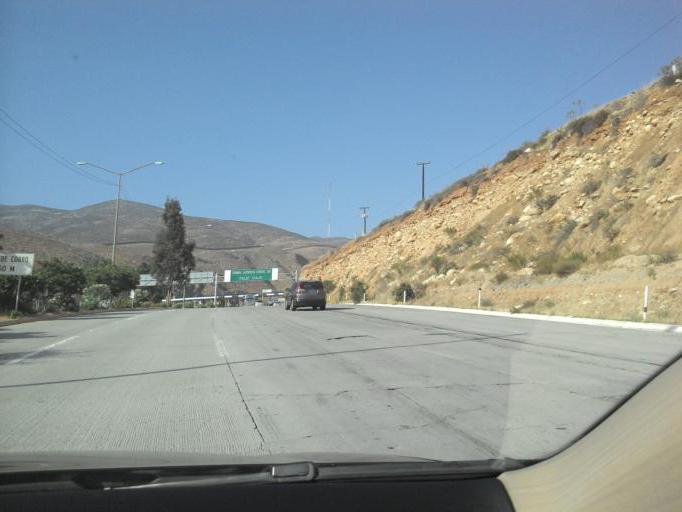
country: MX
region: Baja California
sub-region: Tijuana
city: Ejido Javier Rojo Gomez
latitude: 32.5437
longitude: -116.8535
